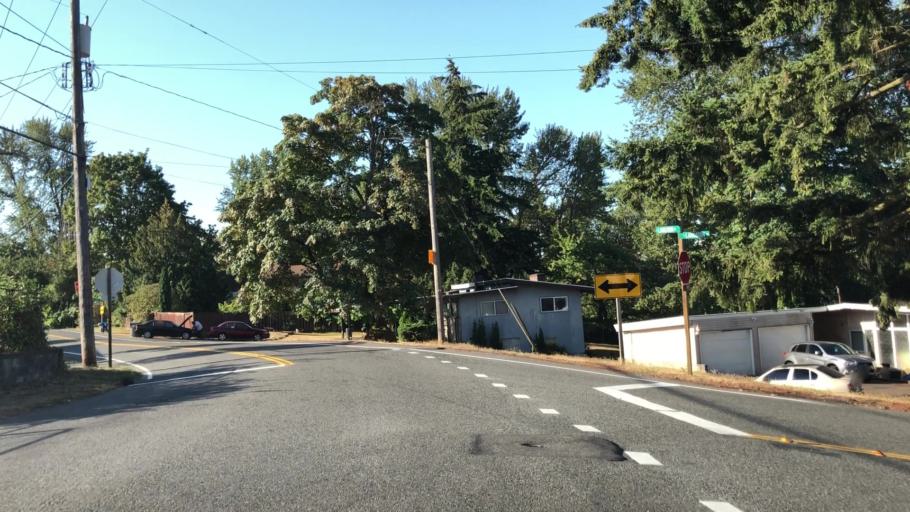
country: US
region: Washington
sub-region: King County
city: Bryn Mawr-Skyway
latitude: 47.4929
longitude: -122.2598
